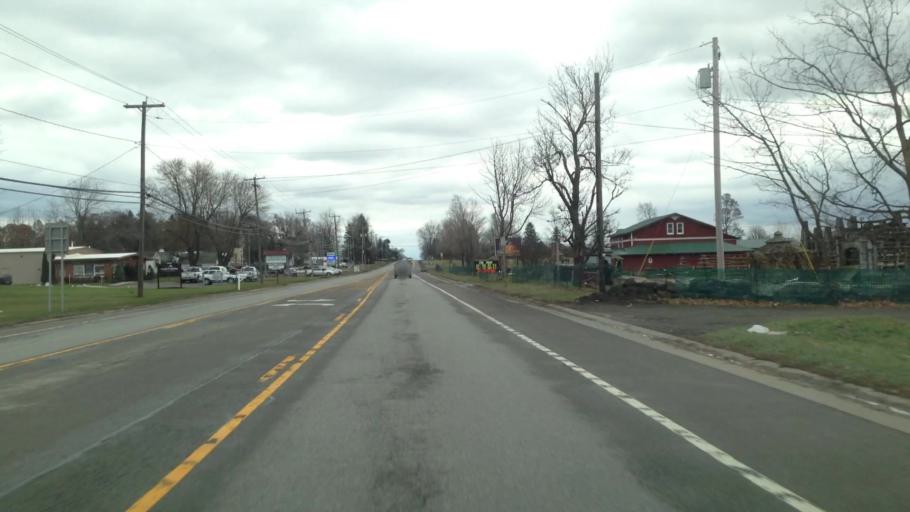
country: US
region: New York
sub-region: Erie County
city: Clarence
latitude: 42.9846
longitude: -78.5701
